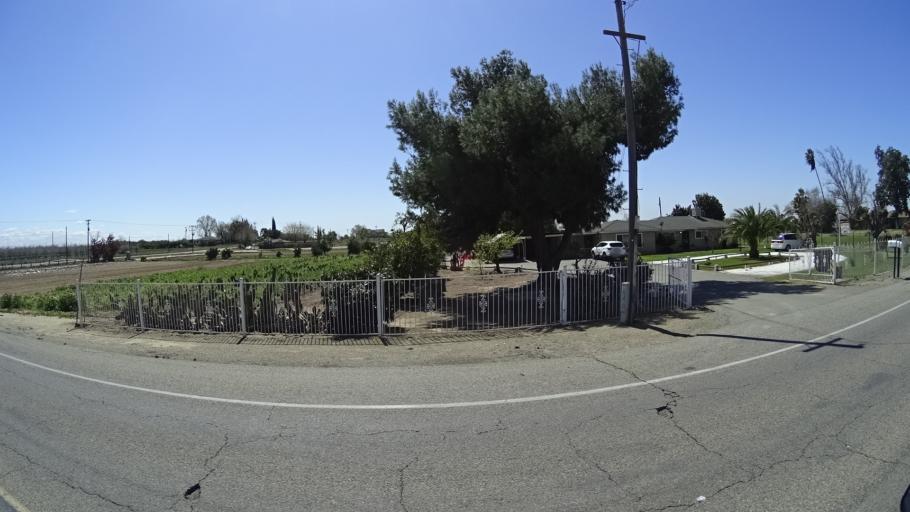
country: US
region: California
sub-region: Fresno County
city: West Park
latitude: 36.7065
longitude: -119.8634
